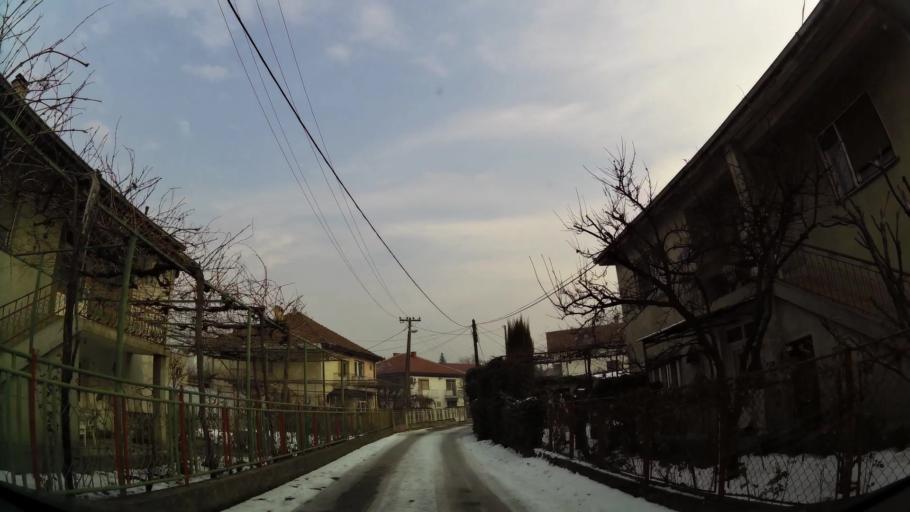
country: MK
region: Kisela Voda
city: Kisela Voda
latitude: 41.9966
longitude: 21.5035
